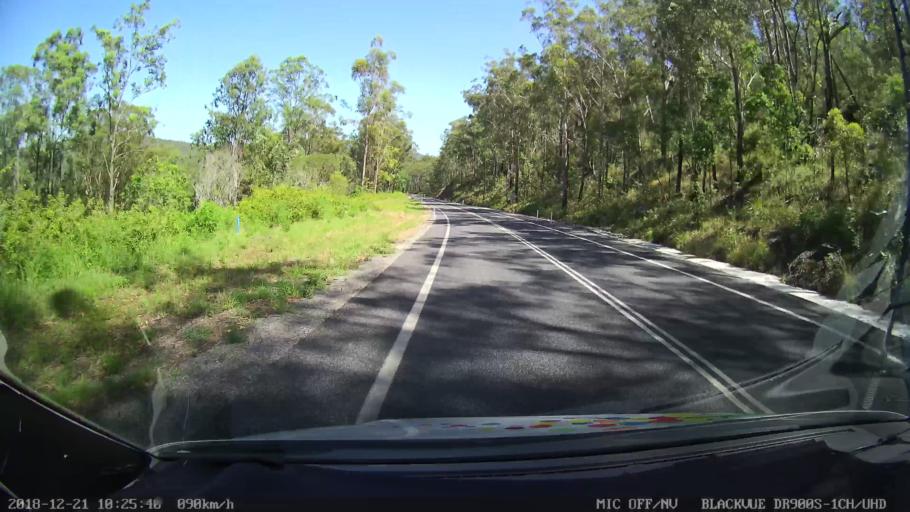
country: AU
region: New South Wales
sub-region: Clarence Valley
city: South Grafton
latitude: -29.6326
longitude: 152.7619
